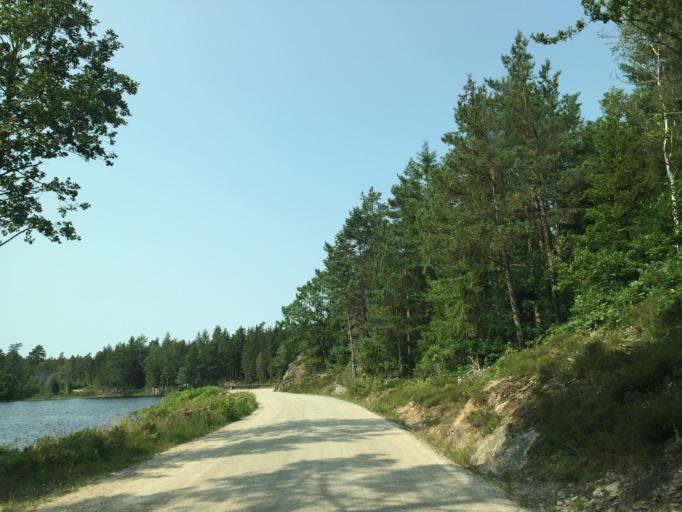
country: SE
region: Vaestra Goetaland
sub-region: Lilla Edets Kommun
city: Lilla Edet
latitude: 58.2296
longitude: 12.1162
